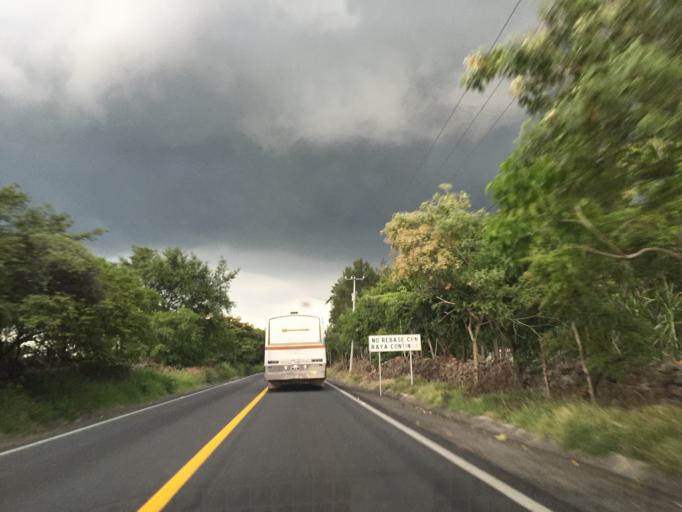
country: MX
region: Colima
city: Cuauhtemoc
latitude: 19.3389
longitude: -103.5873
